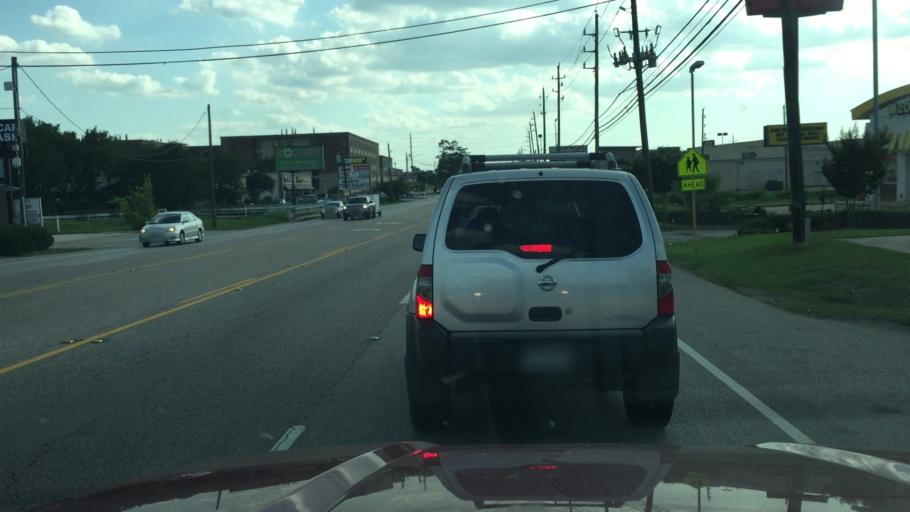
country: US
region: Texas
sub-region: Harris County
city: Spring
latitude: 30.0223
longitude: -95.5217
